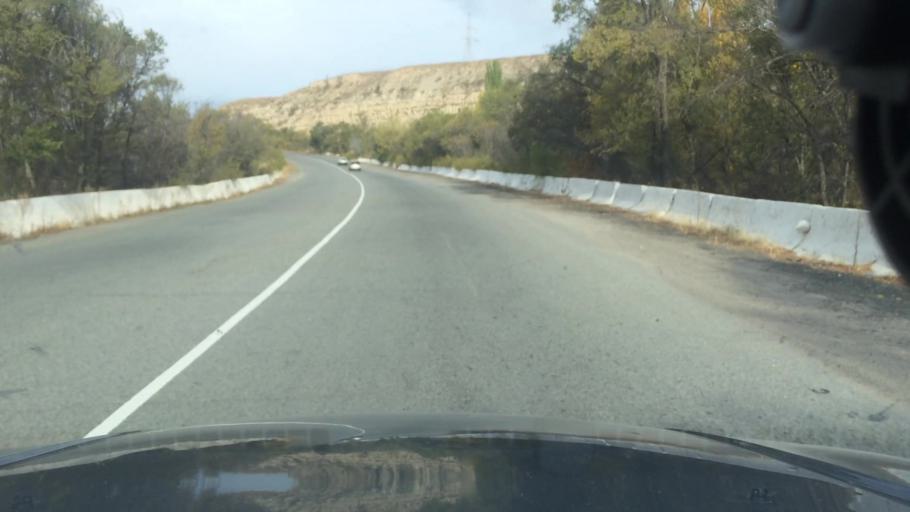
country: KG
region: Ysyk-Koel
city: Karakol
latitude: 42.5940
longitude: 78.3855
